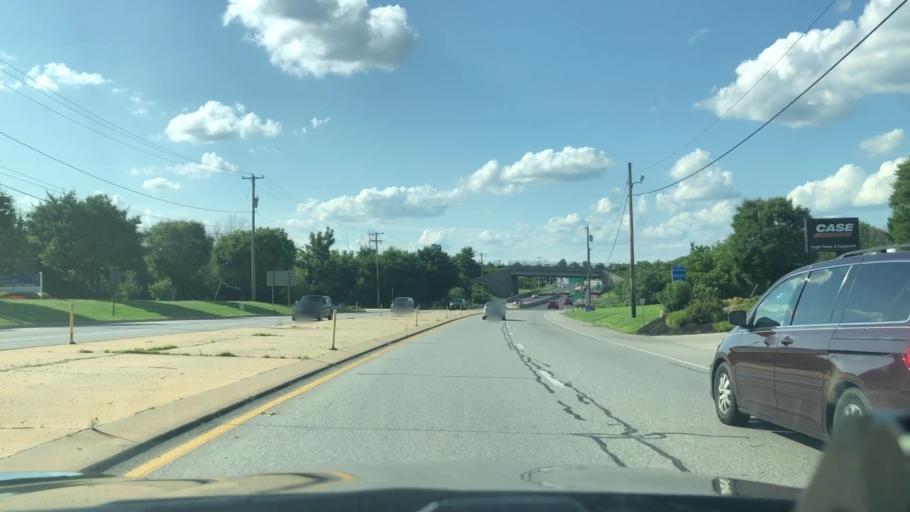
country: US
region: Pennsylvania
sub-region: Montgomery County
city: Montgomeryville
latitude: 40.2292
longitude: -75.2369
